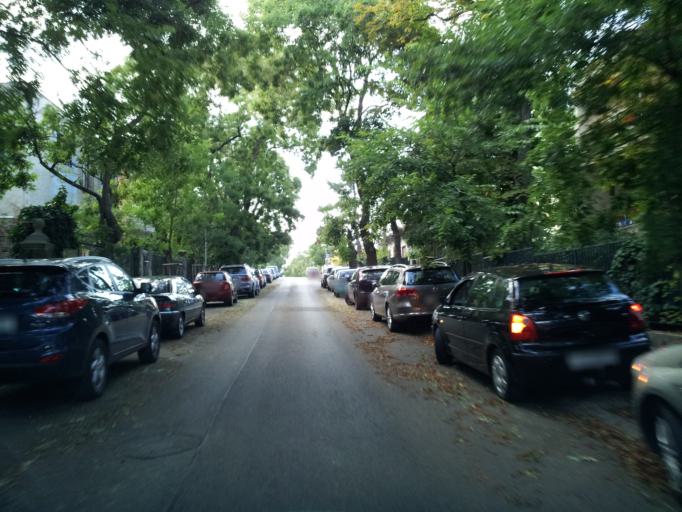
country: HU
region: Budapest
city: Budapest XII. keruelet
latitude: 47.5030
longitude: 19.0166
